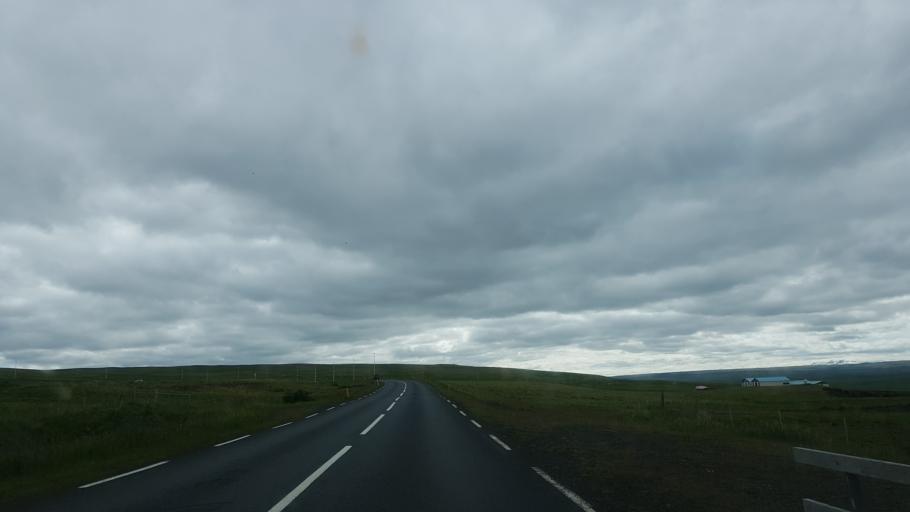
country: IS
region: Northwest
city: Saudarkrokur
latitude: 65.3561
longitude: -20.8885
